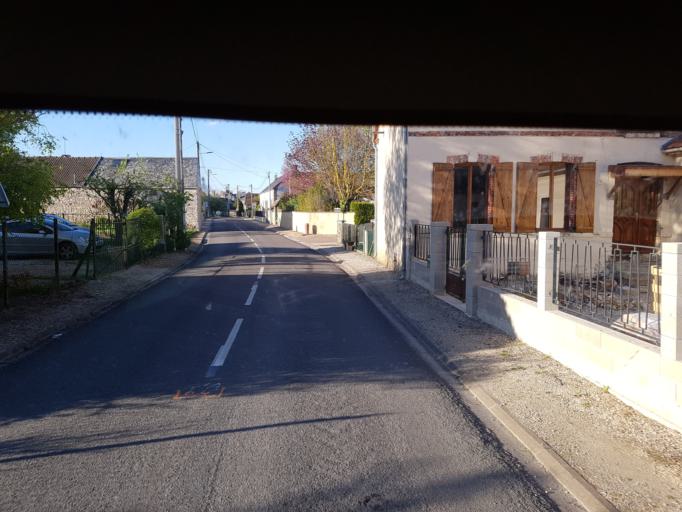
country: FR
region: Champagne-Ardenne
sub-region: Departement de l'Aube
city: Marigny-le-Chatel
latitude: 48.4080
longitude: 3.6609
